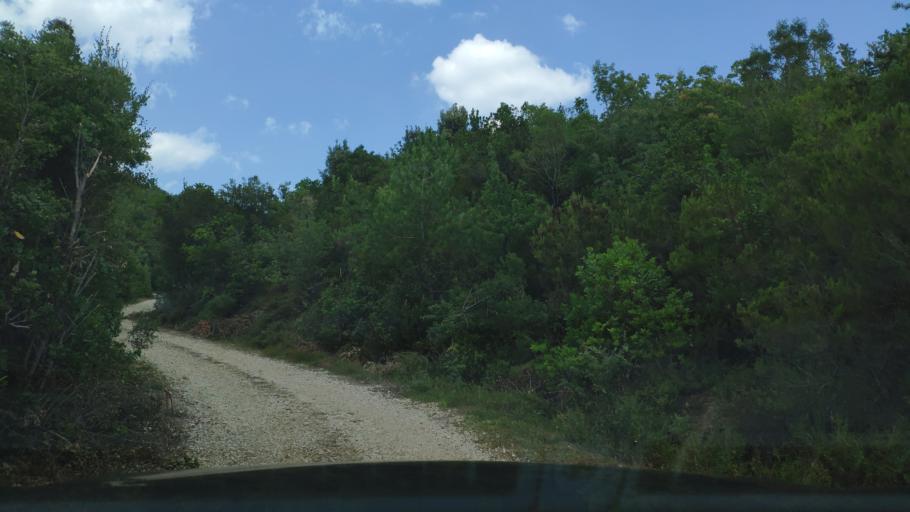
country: GR
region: Epirus
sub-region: Nomos Artas
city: Agios Dimitrios
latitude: 39.3111
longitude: 21.0176
